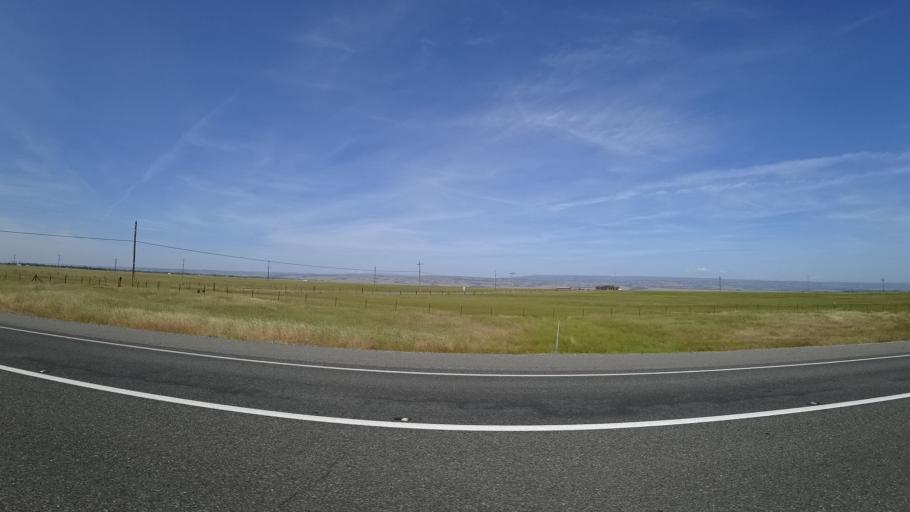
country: US
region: California
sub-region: Tehama County
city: Los Molinos
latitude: 39.9126
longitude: -122.0110
